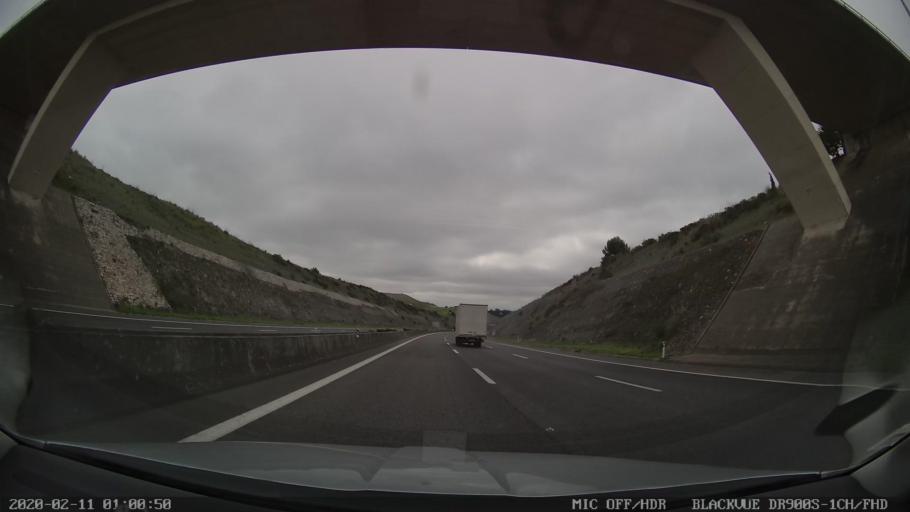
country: PT
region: Lisbon
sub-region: Vila Franca de Xira
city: Sobralinho
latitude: 38.9185
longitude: -9.0740
